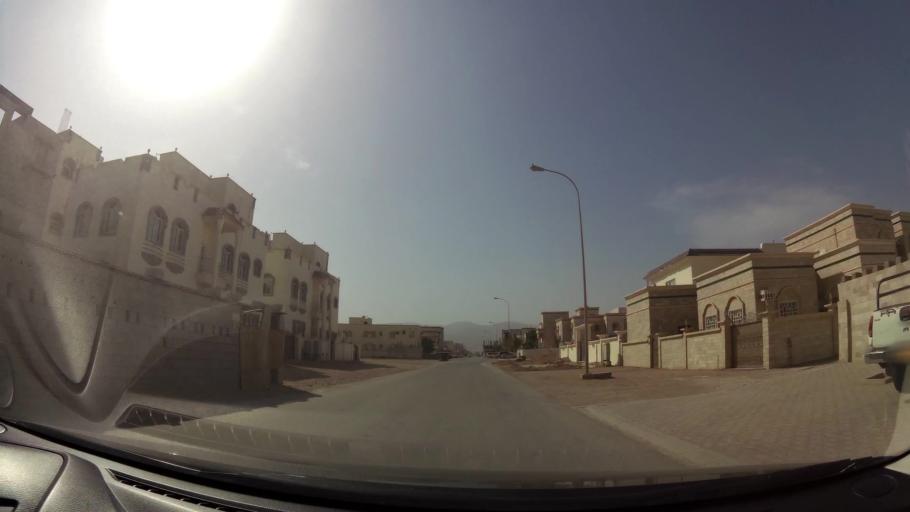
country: OM
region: Zufar
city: Salalah
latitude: 17.0043
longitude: 54.0082
